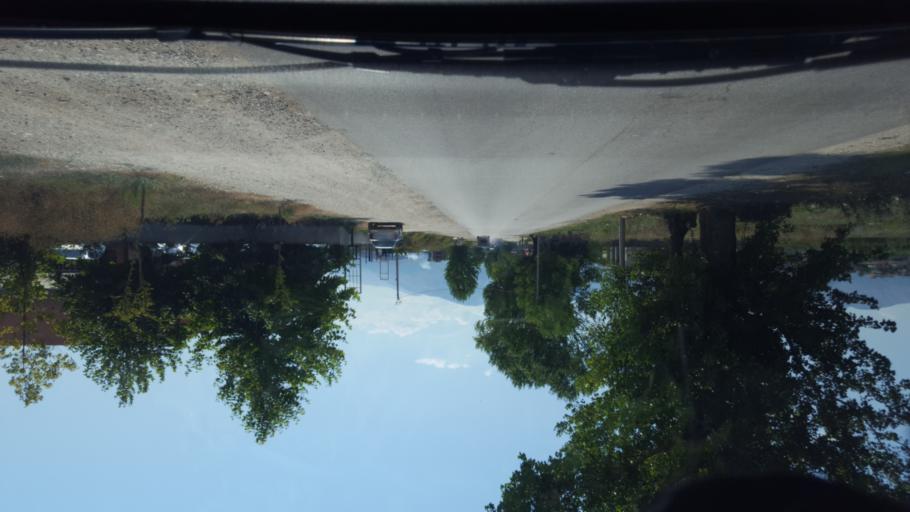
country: AL
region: Vlore
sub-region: Rrethi i Delvines
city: Finiq
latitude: 39.8805
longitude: 20.0380
